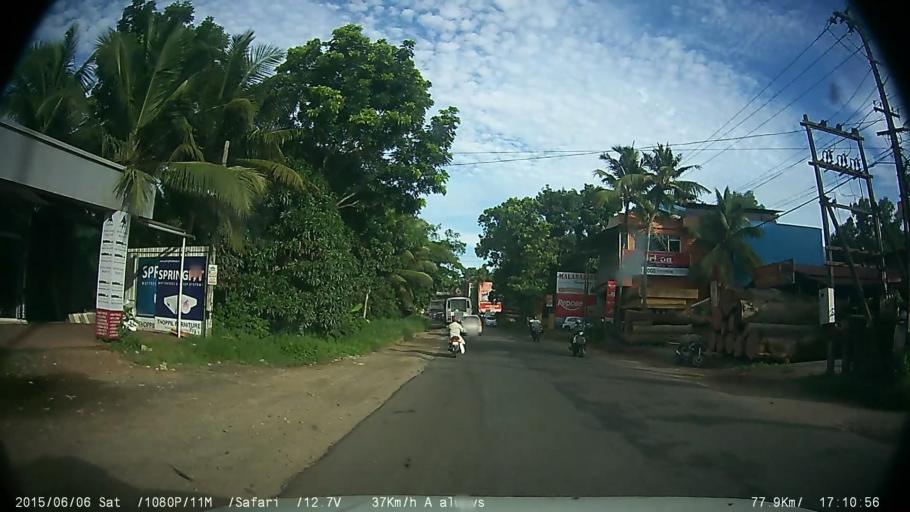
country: IN
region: Kerala
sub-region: Pattanamtitta
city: Tiruvalla
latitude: 9.4059
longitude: 76.5598
